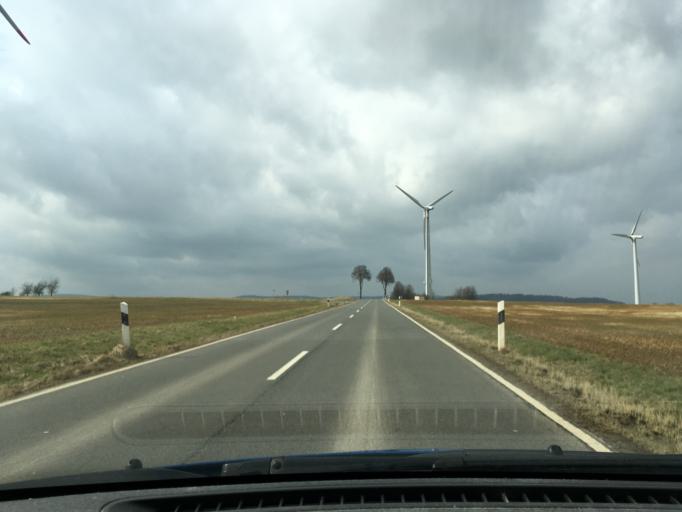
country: DE
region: Lower Saxony
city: Dransfeld
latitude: 51.5113
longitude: 9.7481
